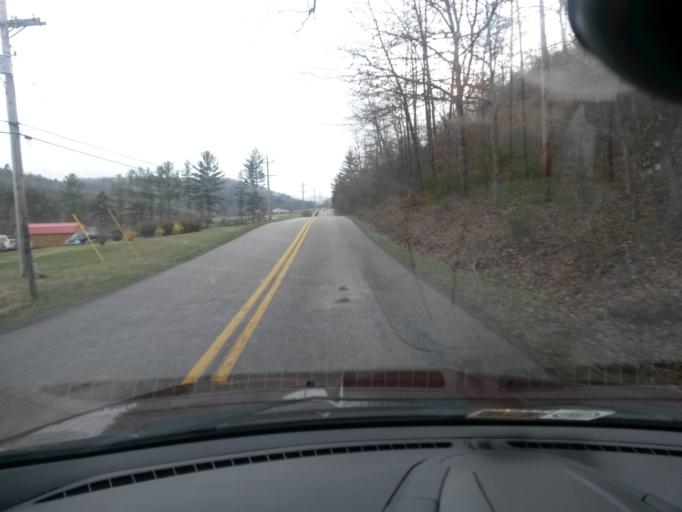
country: US
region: Virginia
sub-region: Bath County
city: Warm Springs
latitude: 37.9920
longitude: -79.8946
